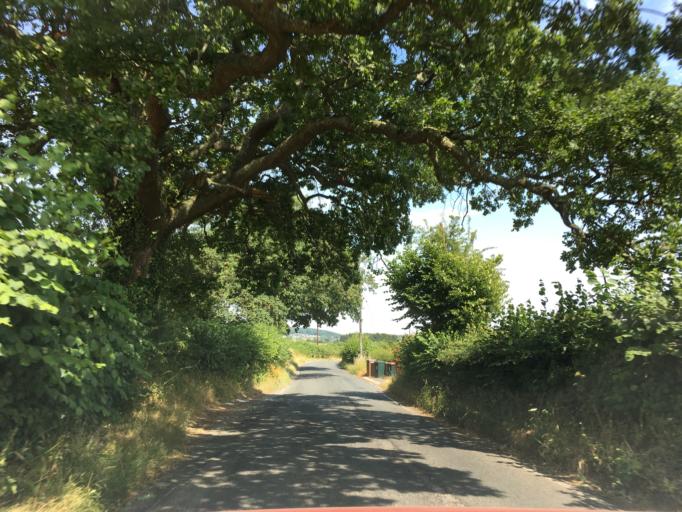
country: GB
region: Wales
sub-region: Newport
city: Langstone
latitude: 51.6128
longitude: -2.8982
